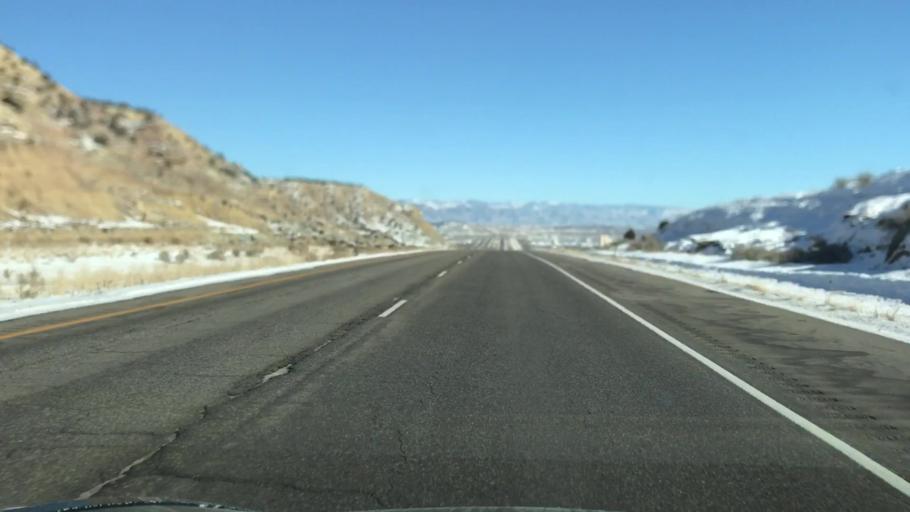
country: US
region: Colorado
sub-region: Garfield County
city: Rifle
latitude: 39.5080
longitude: -107.8806
